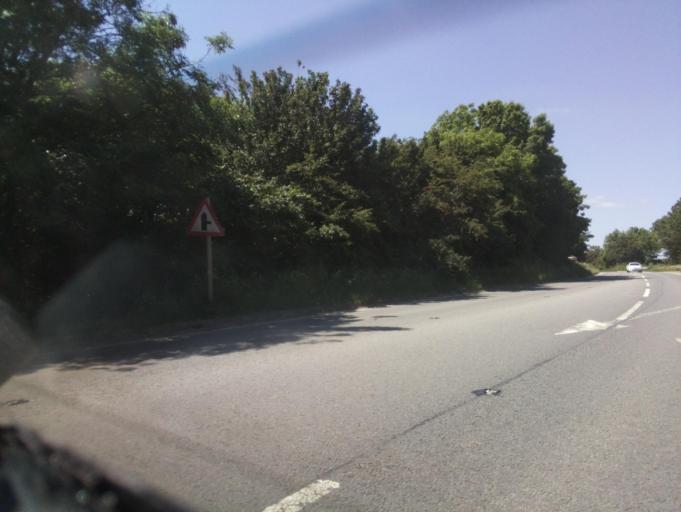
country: GB
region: England
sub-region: Wiltshire
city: Lydiard Tregoze
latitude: 51.5401
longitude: -1.8446
